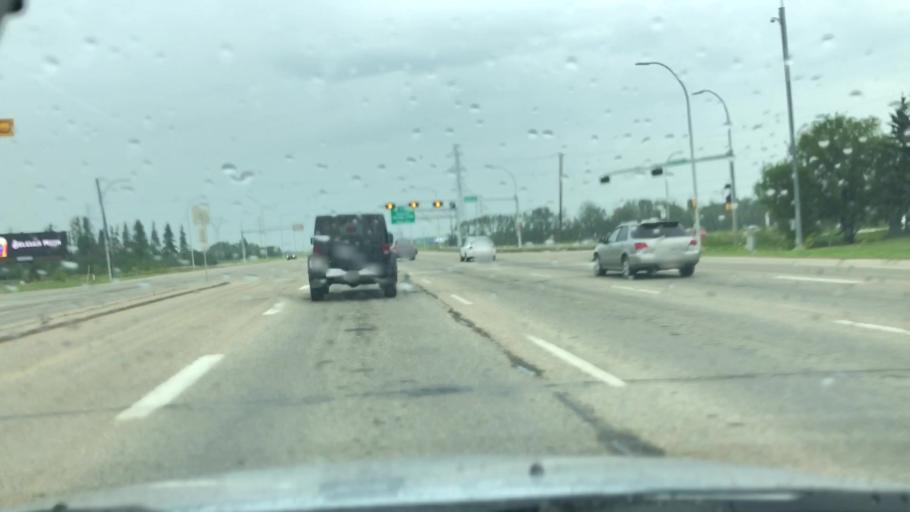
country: CA
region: Alberta
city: St. Albert
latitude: 53.6113
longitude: -113.5905
